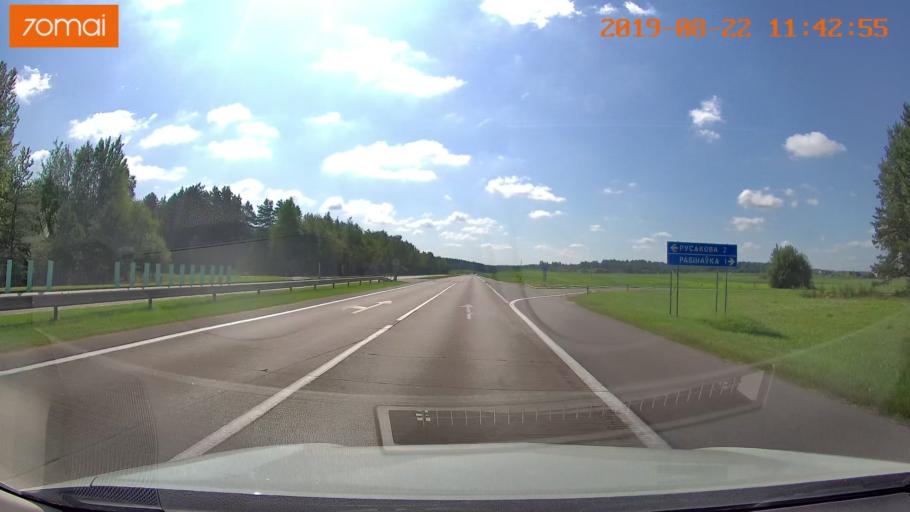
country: BY
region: Minsk
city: Samakhvalavichy
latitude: 53.5563
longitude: 27.4747
